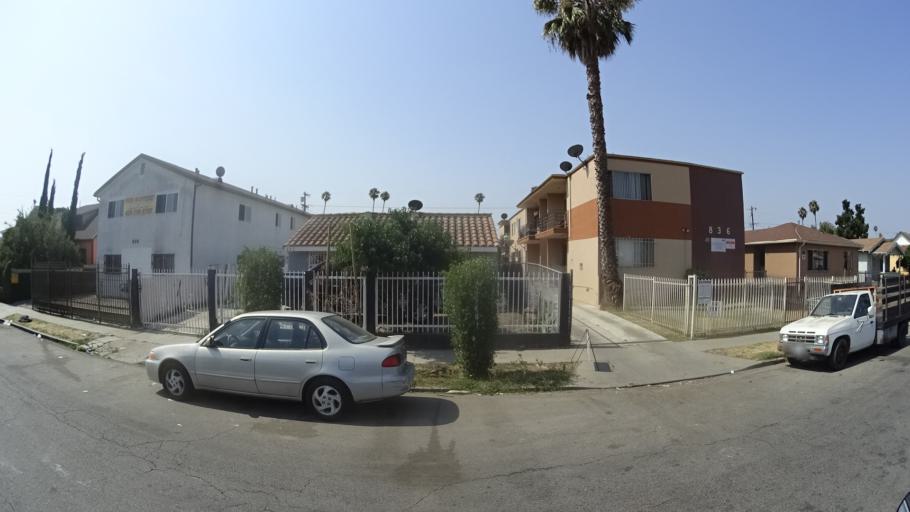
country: US
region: California
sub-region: Los Angeles County
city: Westmont
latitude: 33.9678
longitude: -118.2882
